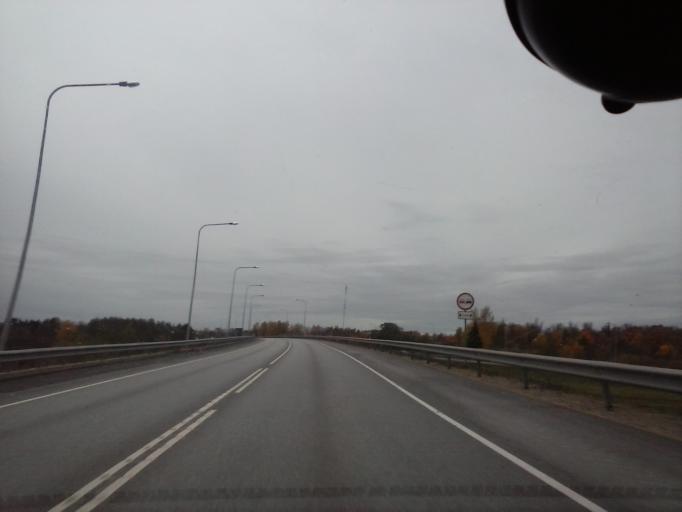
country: EE
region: Jogevamaa
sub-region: Jogeva linn
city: Jogeva
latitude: 58.5677
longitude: 26.2899
